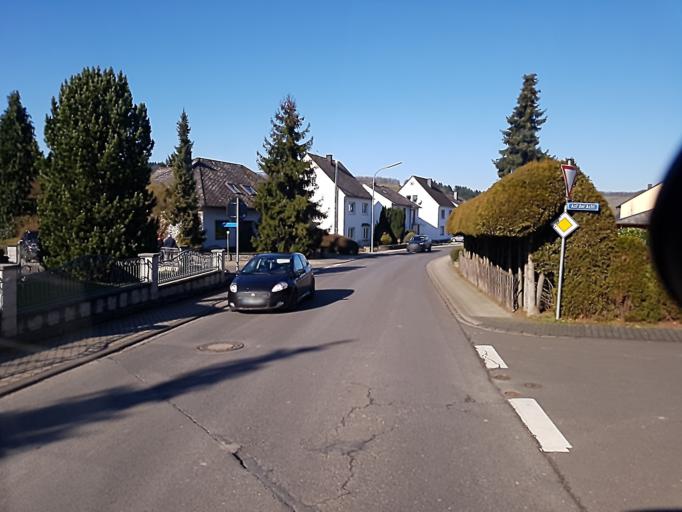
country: DE
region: Rheinland-Pfalz
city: Lieser
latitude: 49.9076
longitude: 7.0084
